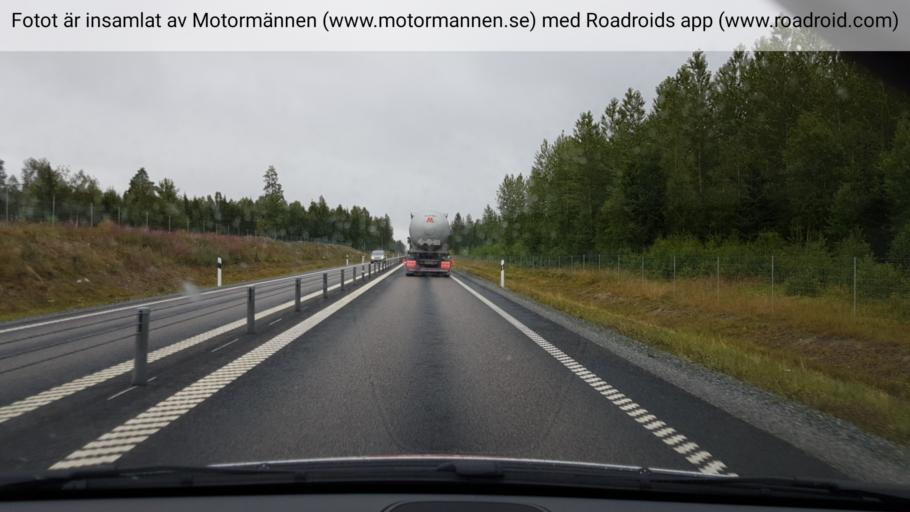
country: SE
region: Uppsala
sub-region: Heby Kommun
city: Heby
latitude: 59.9830
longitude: 16.8537
